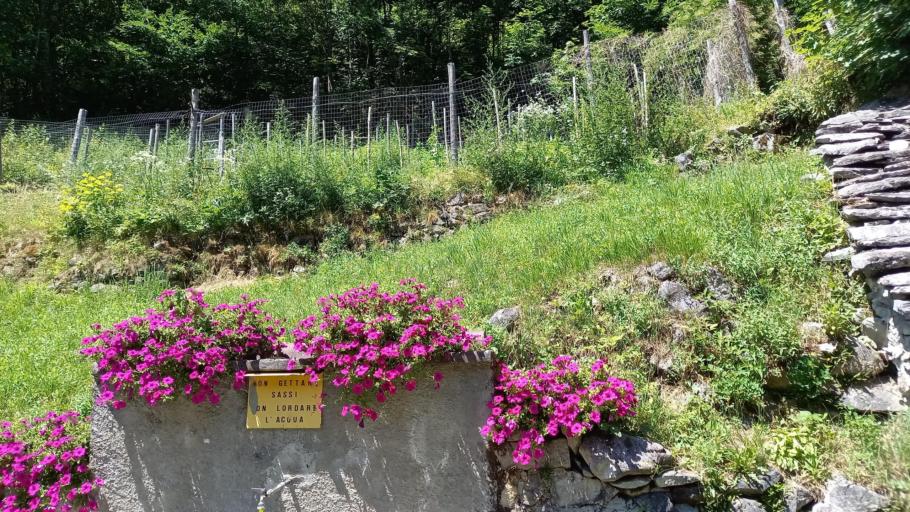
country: IT
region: Lombardy
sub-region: Provincia di Sondrio
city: Novate Mezzola
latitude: 46.2384
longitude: 9.4730
